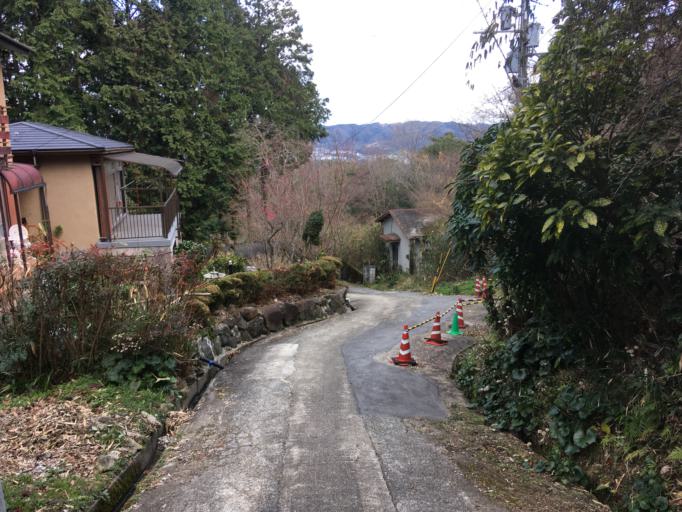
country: JP
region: Nara
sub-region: Ikoma-shi
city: Ikoma
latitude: 34.6752
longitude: 135.6928
